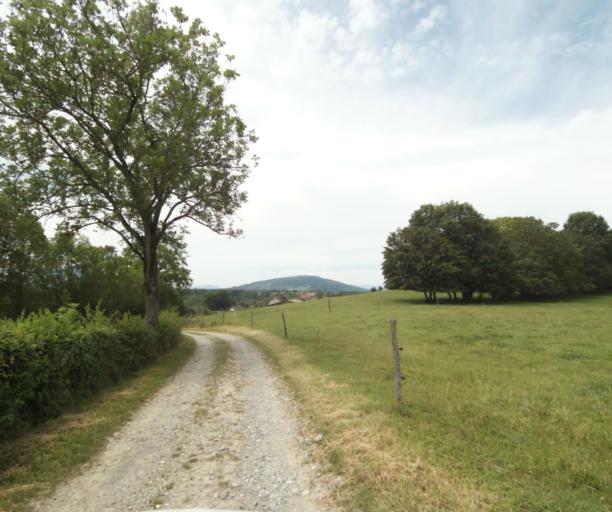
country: FR
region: Rhone-Alpes
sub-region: Departement de la Haute-Savoie
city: Margencel
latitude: 46.3404
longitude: 6.4253
